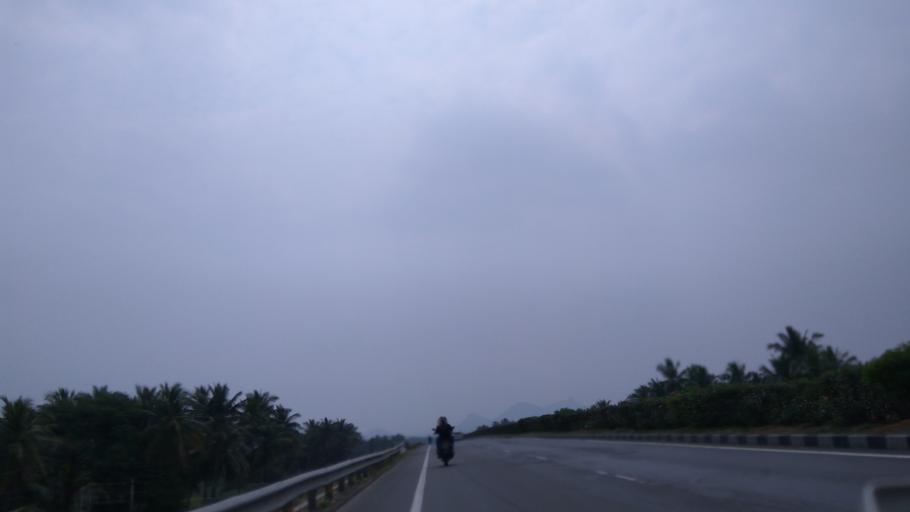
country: IN
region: Tamil Nadu
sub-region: Krishnagiri
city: Kaverippattanam
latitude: 12.4335
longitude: 78.2236
